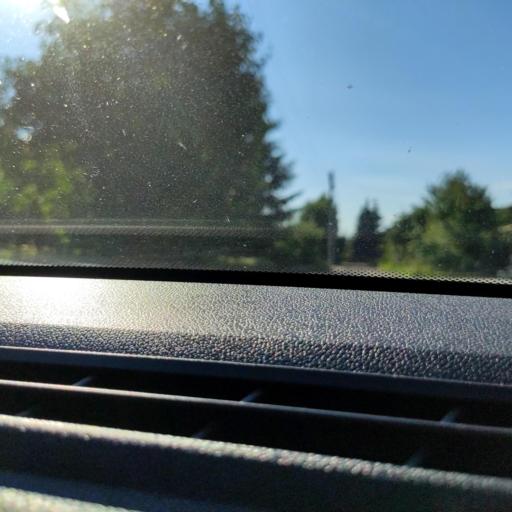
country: RU
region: Samara
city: Podstepki
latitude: 53.5698
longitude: 49.0684
